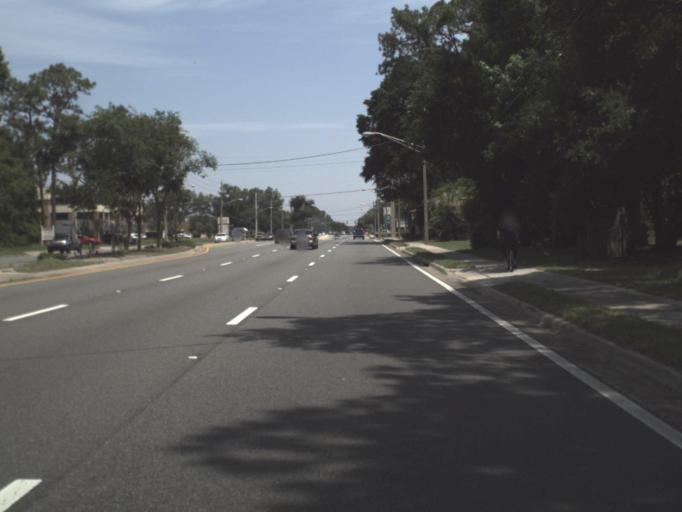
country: US
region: Florida
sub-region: Saint Johns County
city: Fruit Cove
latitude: 30.1429
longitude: -81.6325
